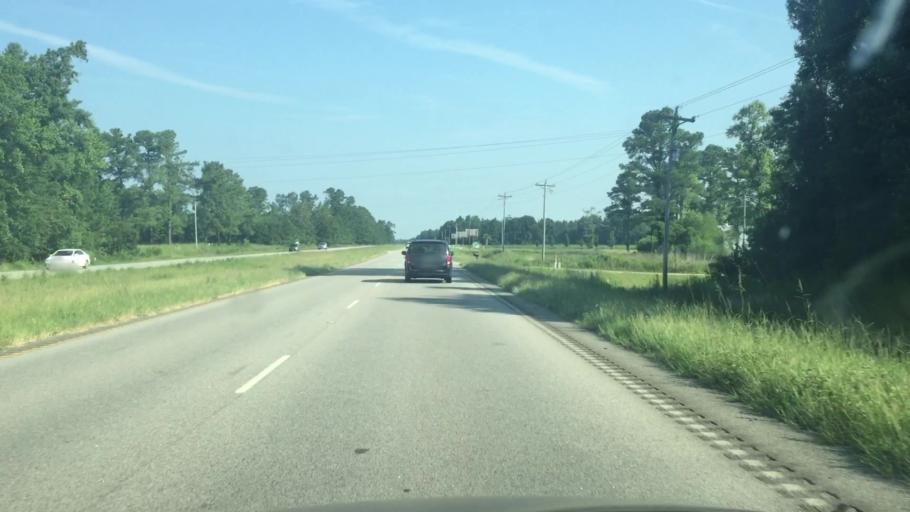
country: US
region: South Carolina
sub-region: Horry County
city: Little River
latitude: 33.9668
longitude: -78.7395
